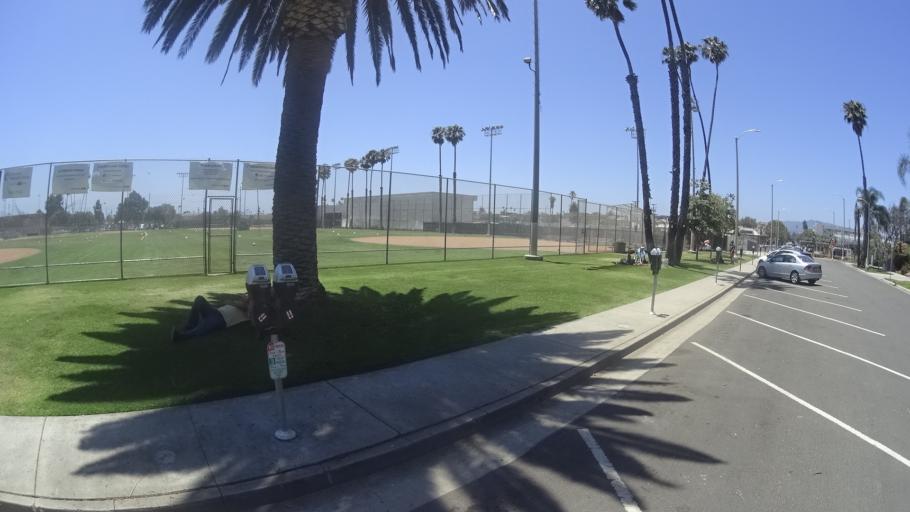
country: US
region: California
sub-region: Los Angeles County
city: Santa Monica
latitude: 34.0219
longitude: -118.4797
